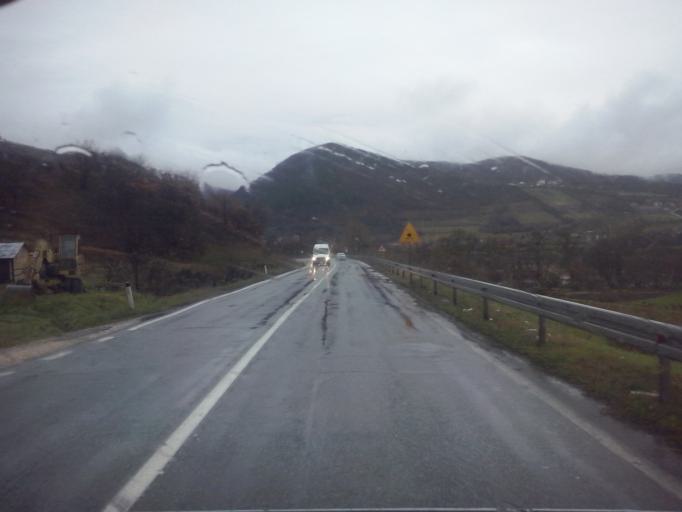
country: RS
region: Central Serbia
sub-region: Raski Okrug
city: Raska
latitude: 43.3315
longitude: 20.6322
